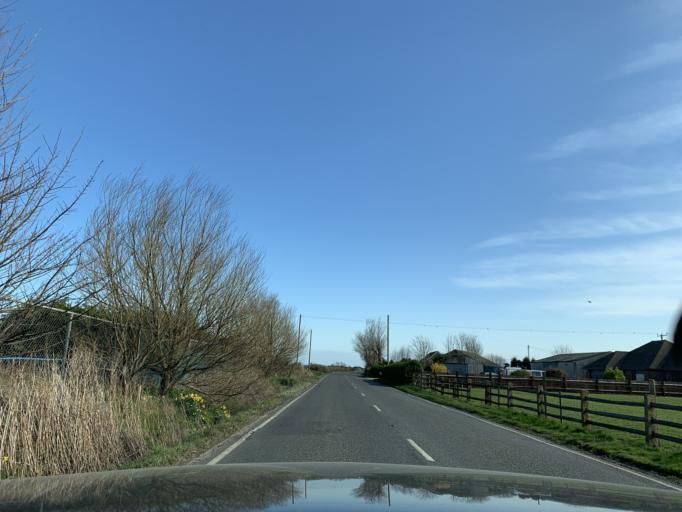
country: GB
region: England
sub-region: Kent
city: Lydd
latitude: 50.9503
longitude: 0.9149
